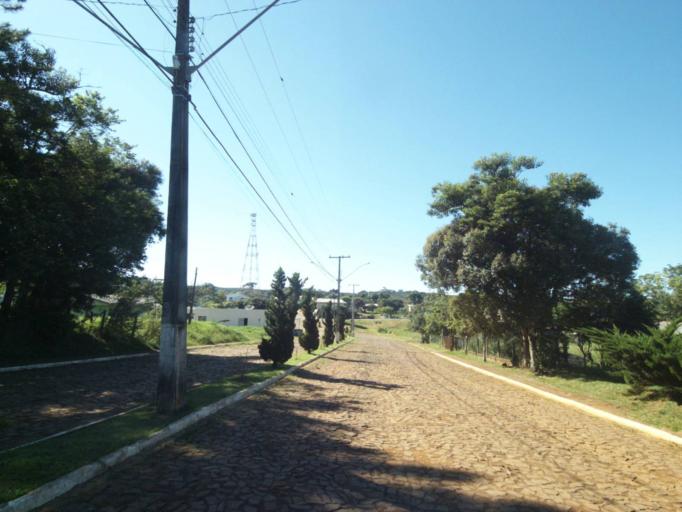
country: BR
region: Parana
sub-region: Pinhao
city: Pinhao
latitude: -25.8370
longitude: -52.0295
